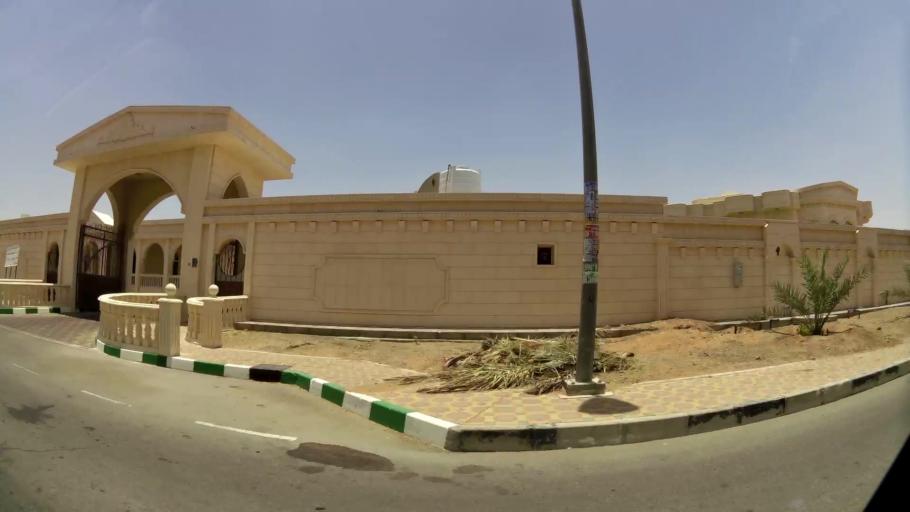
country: OM
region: Al Buraimi
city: Al Buraymi
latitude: 24.2695
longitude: 55.7314
